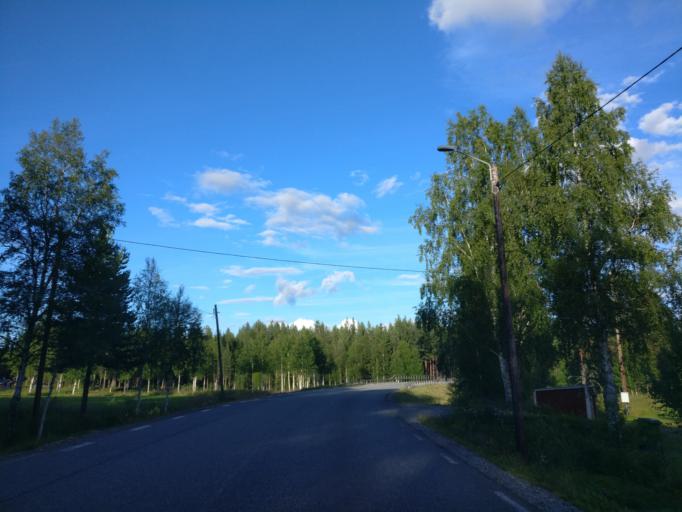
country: SE
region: Jaemtland
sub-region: Braecke Kommun
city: Braecke
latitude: 62.4591
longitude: 14.9635
